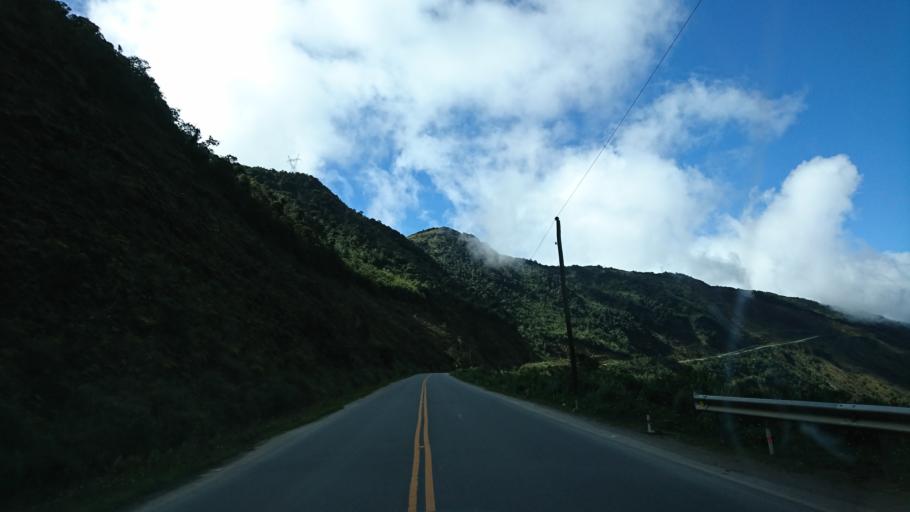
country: BO
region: La Paz
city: Coroico
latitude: -16.2930
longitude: -67.8897
